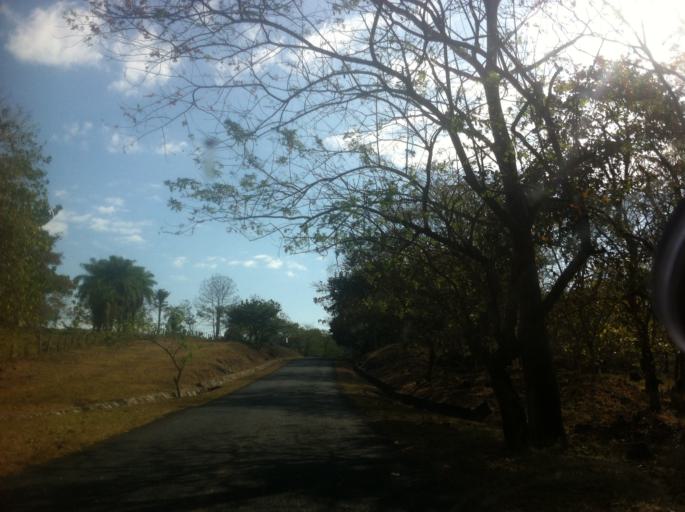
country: NI
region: Rio San Juan
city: San Miguelito
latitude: 11.4321
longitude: -84.8859
